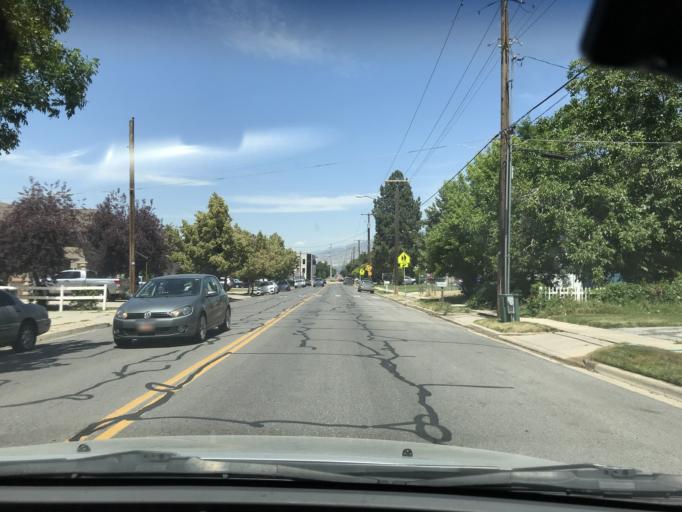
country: US
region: Utah
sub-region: Davis County
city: Woods Cross
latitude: 40.8726
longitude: -111.8857
